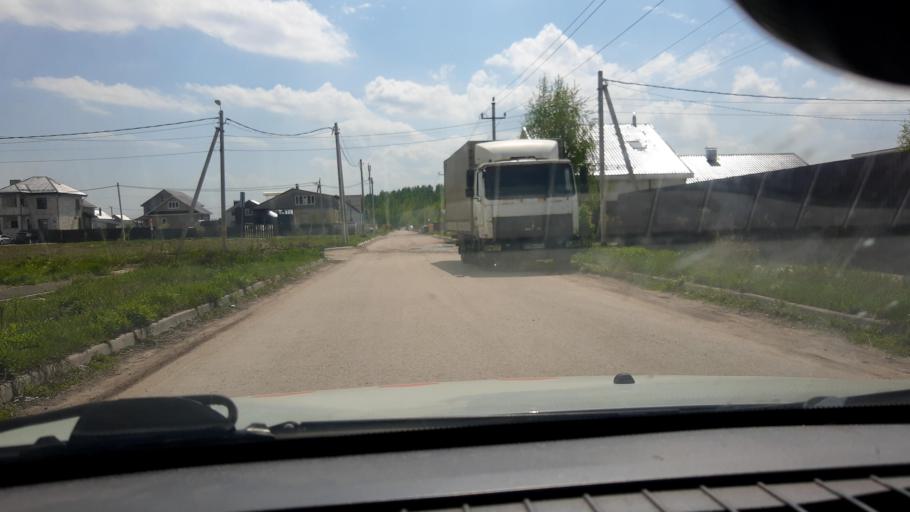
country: RU
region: Nizjnij Novgorod
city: Bor
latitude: 56.3907
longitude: 44.0567
